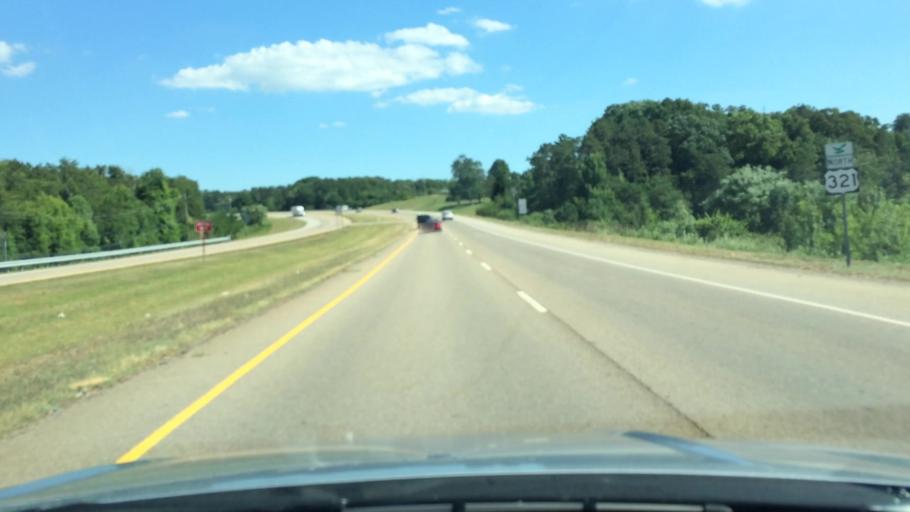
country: US
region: Tennessee
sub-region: Loudon County
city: Lenoir City
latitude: 35.7650
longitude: -84.2292
